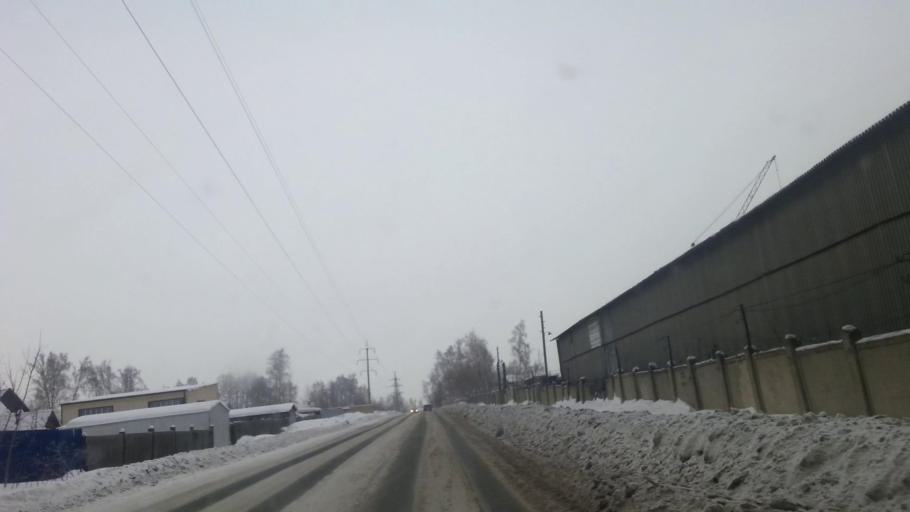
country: RU
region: Altai Krai
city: Novosilikatnyy
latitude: 53.3119
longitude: 83.6186
